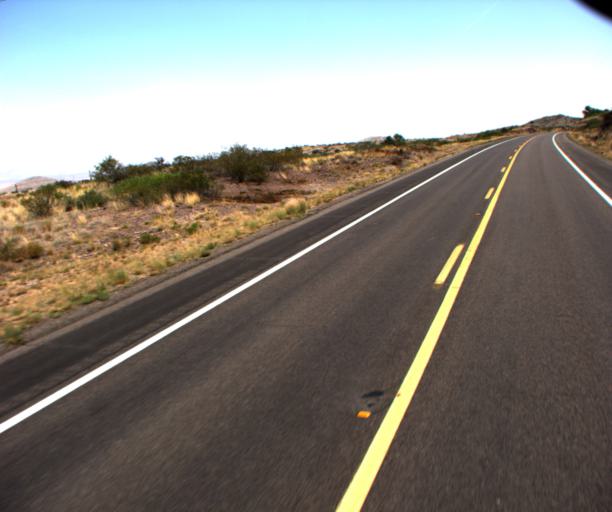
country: US
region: Arizona
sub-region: Greenlee County
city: Clifton
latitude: 32.7621
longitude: -109.2481
